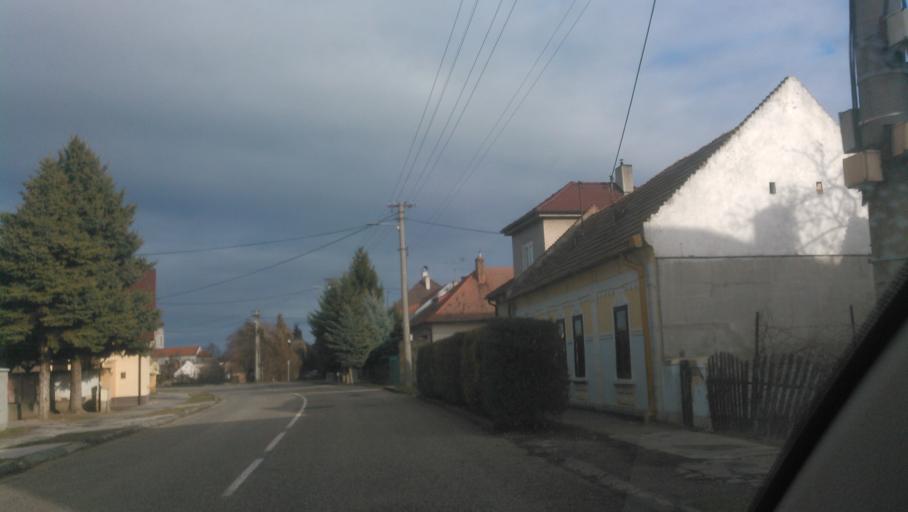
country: SK
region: Trnavsky
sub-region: Okres Trnava
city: Trnava
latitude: 48.3207
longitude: 17.6536
